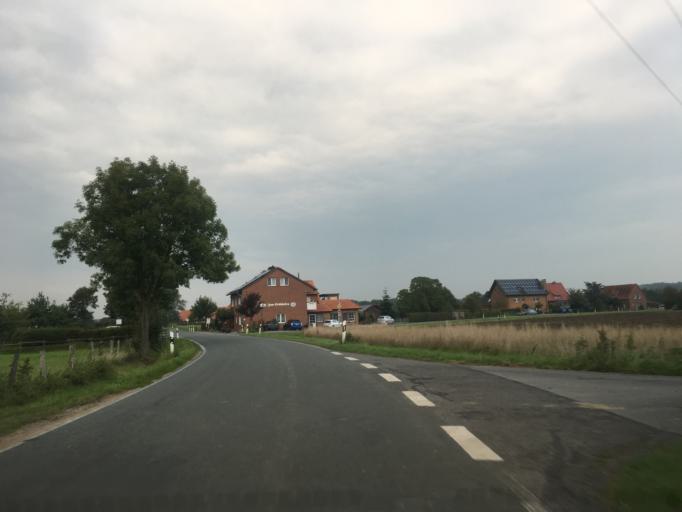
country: DE
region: North Rhine-Westphalia
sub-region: Regierungsbezirk Munster
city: Ascheberg
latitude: 51.7648
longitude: 7.5879
